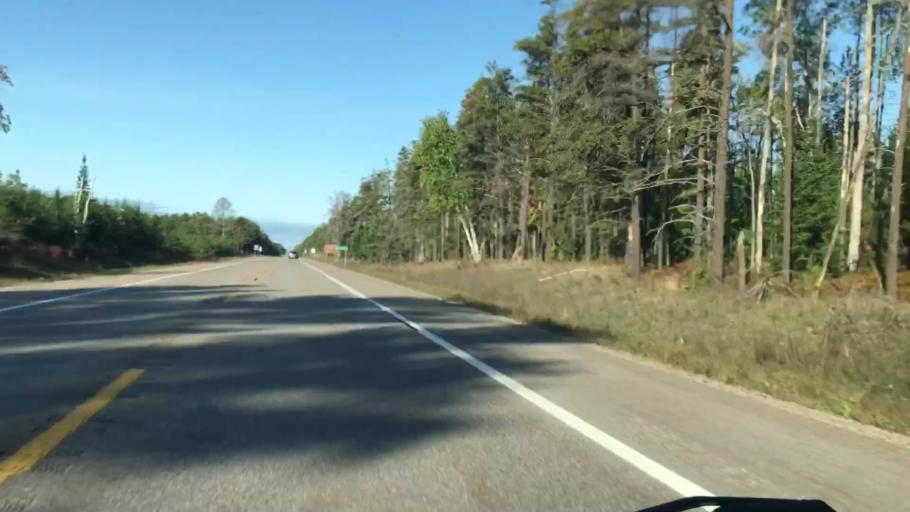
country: US
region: Michigan
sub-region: Chippewa County
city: Sault Ste. Marie
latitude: 46.3703
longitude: -84.7345
